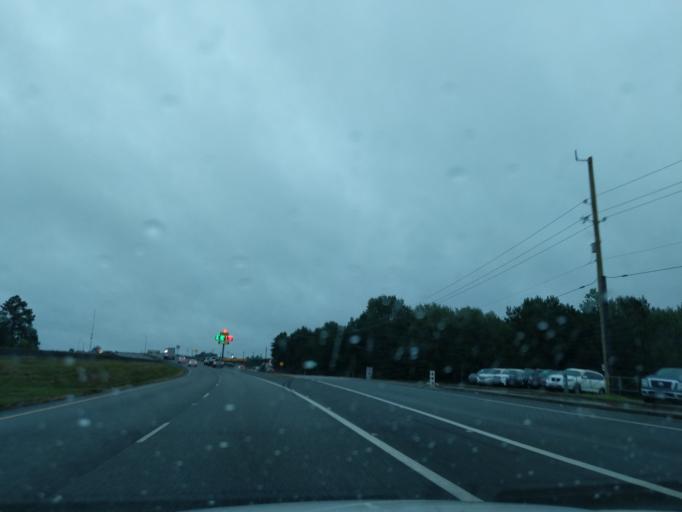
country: US
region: Texas
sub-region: Angelina County
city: Lufkin
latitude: 31.3258
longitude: -94.6924
